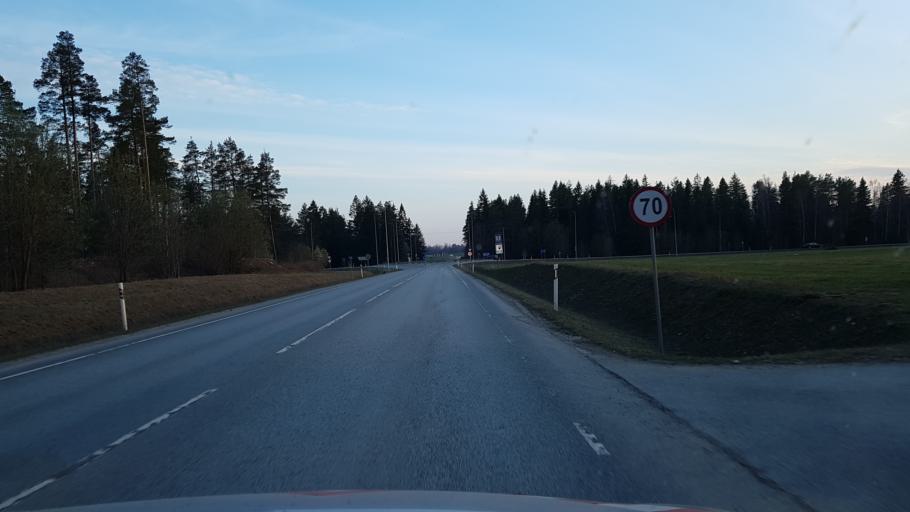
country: EE
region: Laeaene-Virumaa
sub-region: Someru vald
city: Someru
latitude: 59.3337
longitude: 26.4060
